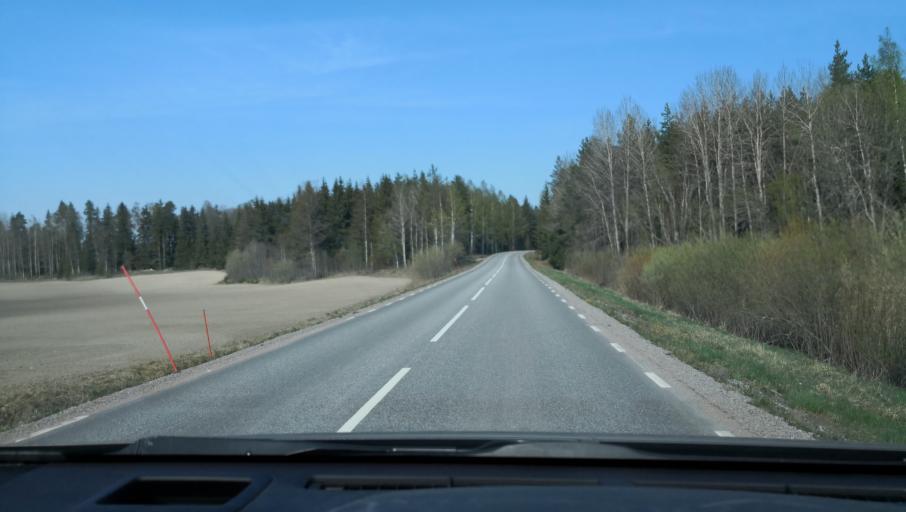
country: SE
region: Vaestmanland
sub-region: Sala Kommun
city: Sala
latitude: 59.9918
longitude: 16.6463
